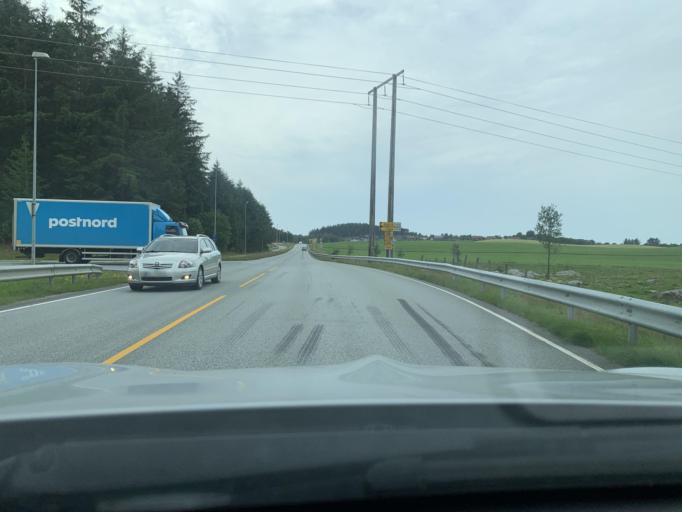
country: NO
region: Rogaland
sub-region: Time
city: Bryne
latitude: 58.7373
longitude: 5.6861
